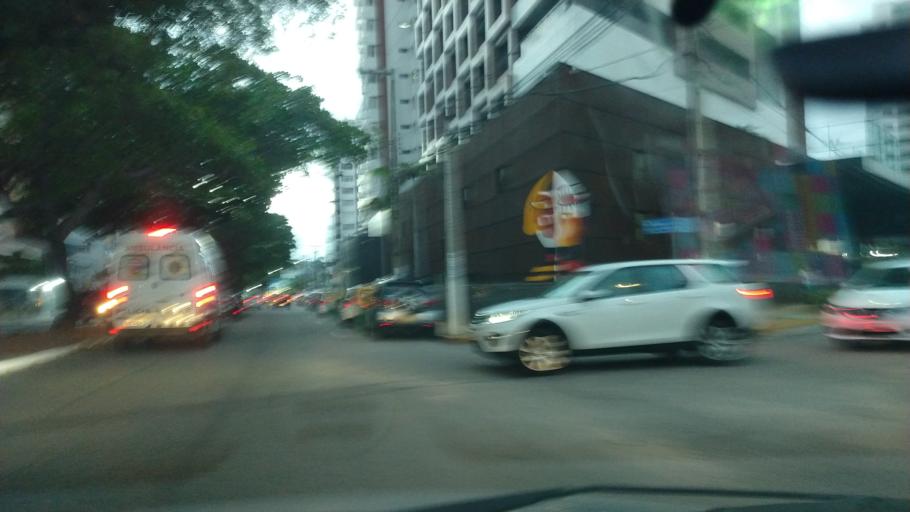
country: BR
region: Rio Grande do Norte
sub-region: Natal
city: Natal
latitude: -5.7821
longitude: -35.1982
